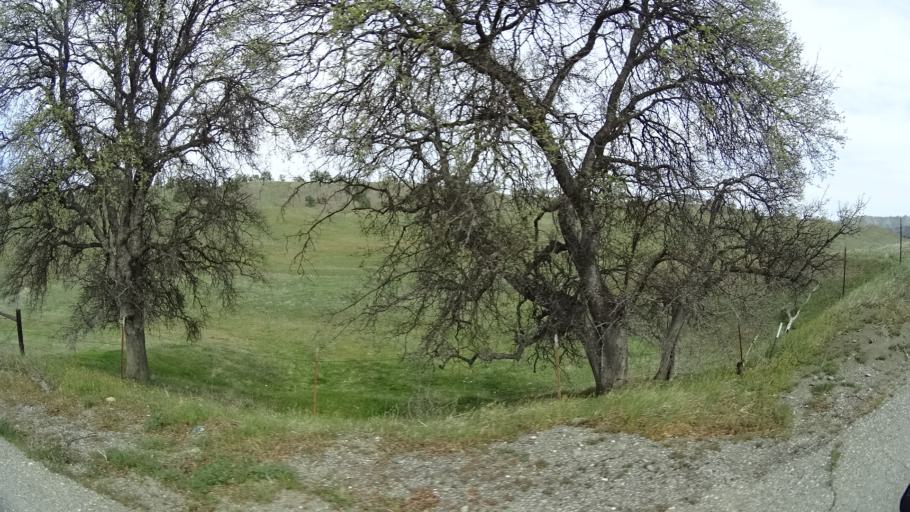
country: US
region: California
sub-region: Glenn County
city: Willows
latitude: 39.6121
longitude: -122.5667
